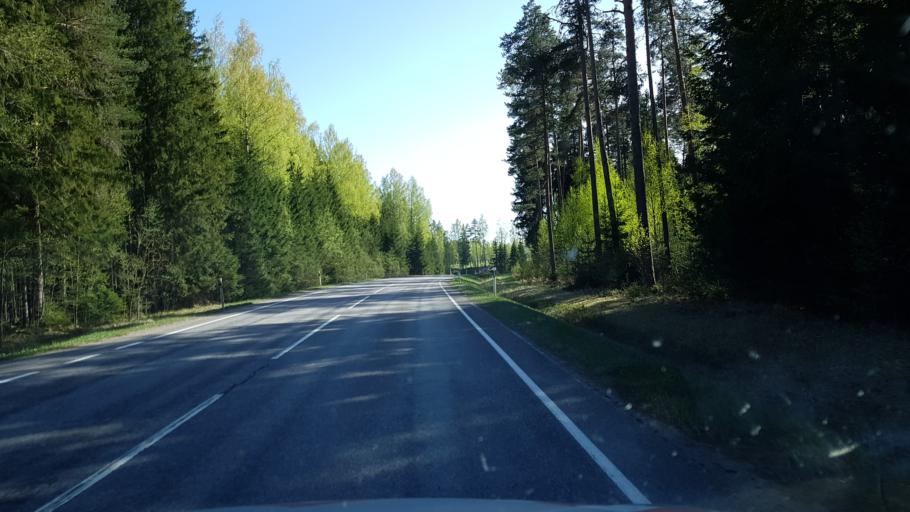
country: EE
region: Paernumaa
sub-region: Saarde vald
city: Kilingi-Nomme
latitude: 58.1853
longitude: 25.0539
